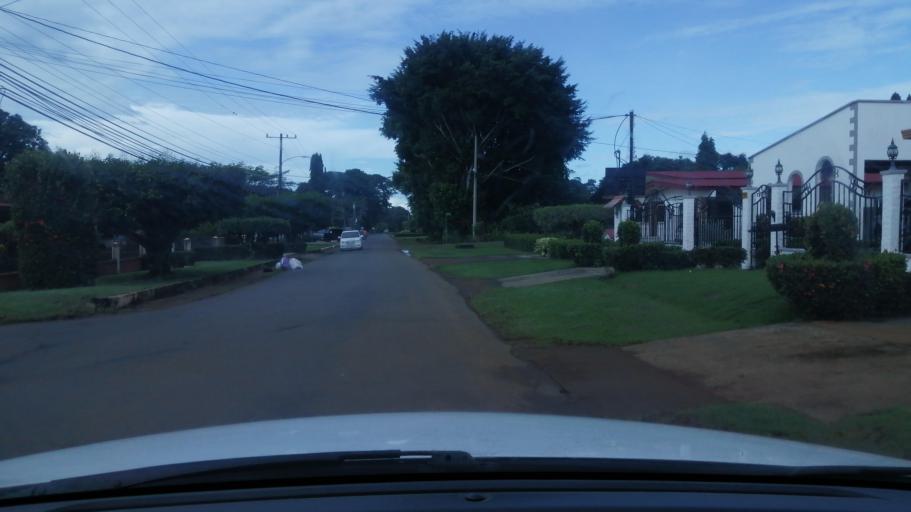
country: PA
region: Chiriqui
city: El Quiteno
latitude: 8.4589
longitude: -82.4181
